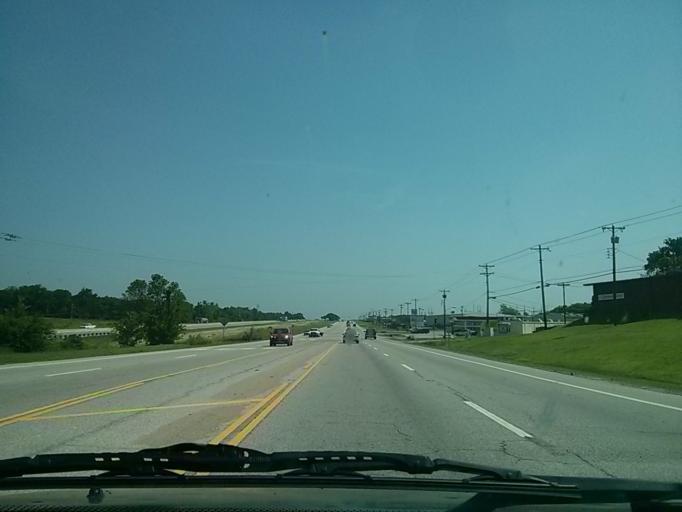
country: US
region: Oklahoma
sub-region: Tulsa County
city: Oakhurst
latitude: 36.0474
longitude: -96.0779
